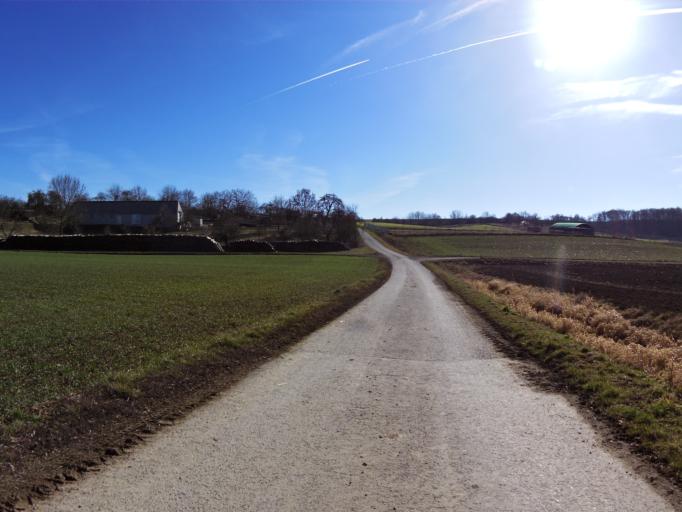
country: DE
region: Bavaria
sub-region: Regierungsbezirk Unterfranken
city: Kurnach
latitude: 49.8563
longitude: 10.0101
